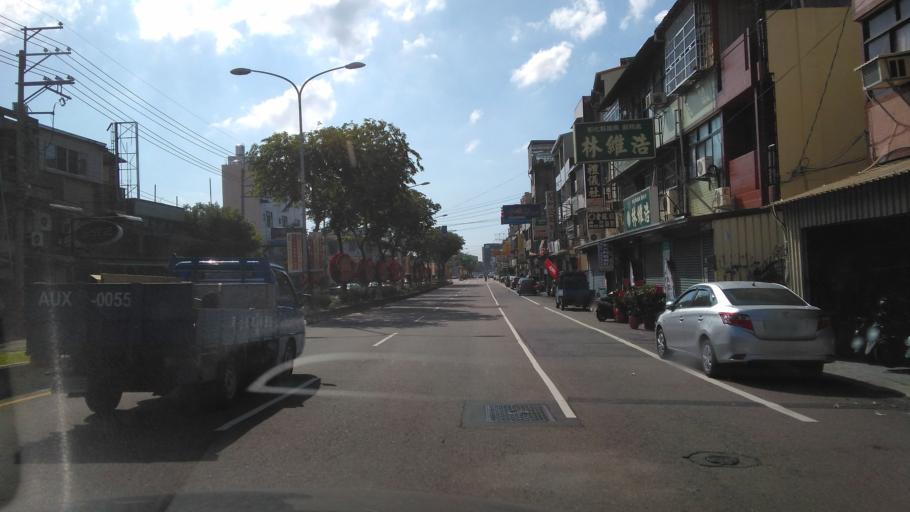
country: TW
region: Taiwan
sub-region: Changhua
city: Chang-hua
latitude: 24.0829
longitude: 120.5917
